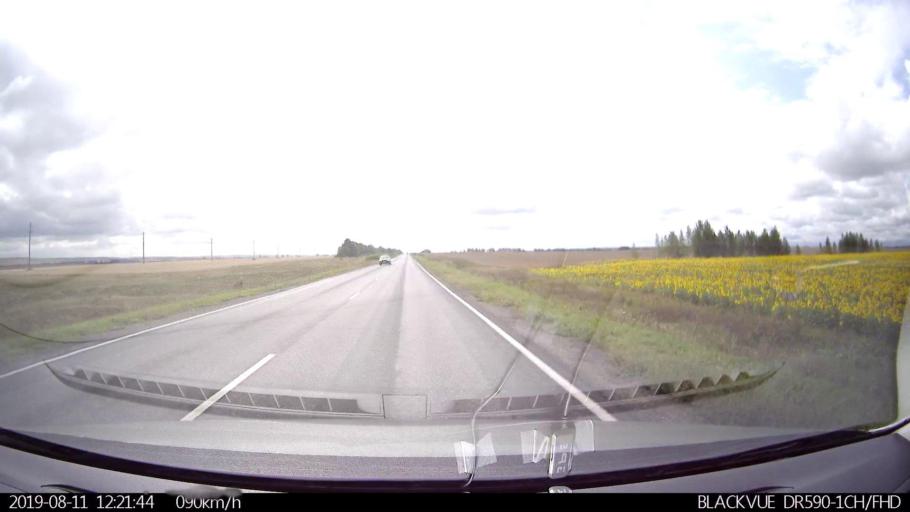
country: RU
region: Ulyanovsk
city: Ignatovka
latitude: 53.9172
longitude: 47.9568
